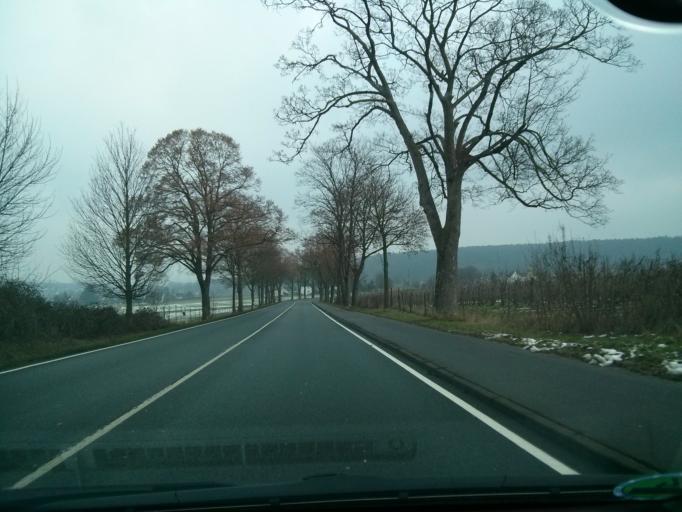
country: DE
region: North Rhine-Westphalia
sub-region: Regierungsbezirk Koln
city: Alfter
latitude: 50.6981
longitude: 7.0100
